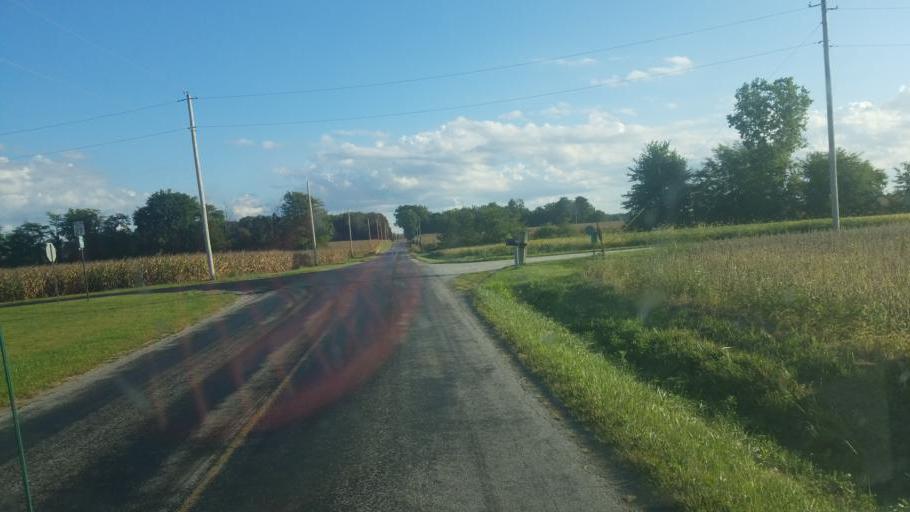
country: US
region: Ohio
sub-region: Wyandot County
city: Carey
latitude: 40.9202
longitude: -83.4009
